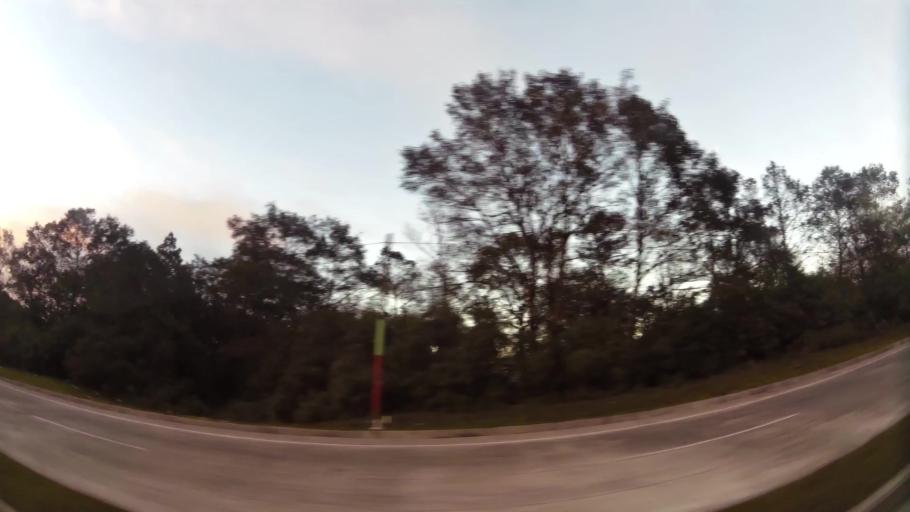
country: GT
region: Solola
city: Concepcion
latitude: 14.8361
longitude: -91.1084
